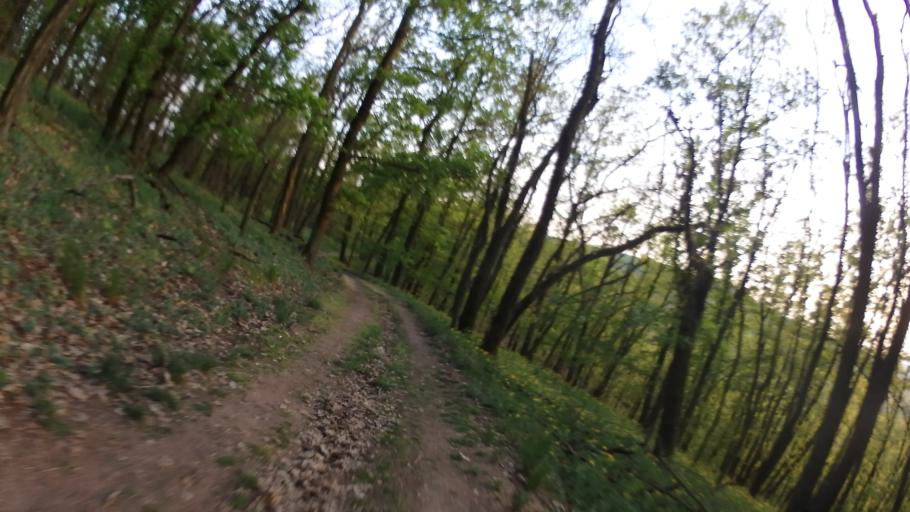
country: CZ
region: South Moravian
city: Ostopovice
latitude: 49.1508
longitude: 16.5300
